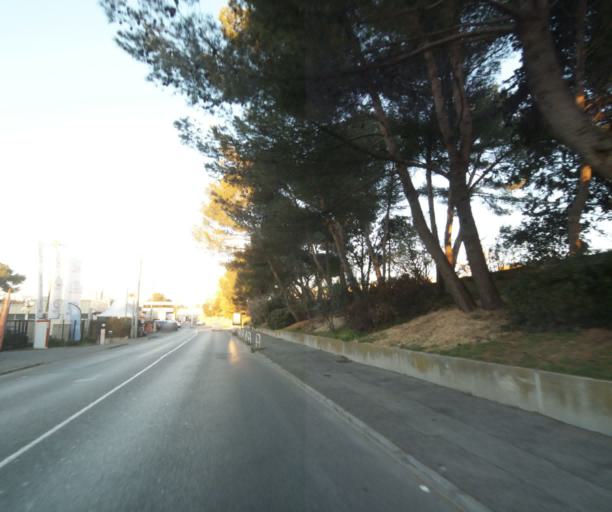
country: FR
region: Provence-Alpes-Cote d'Azur
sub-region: Departement des Alpes-Maritimes
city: Biot
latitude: 43.6025
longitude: 7.0905
